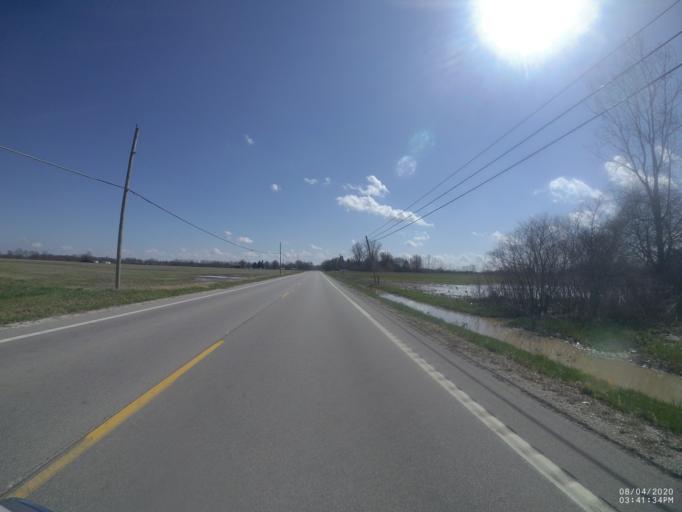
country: US
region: Ohio
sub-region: Sandusky County
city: Stony Prairie
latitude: 41.2594
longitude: -83.2356
